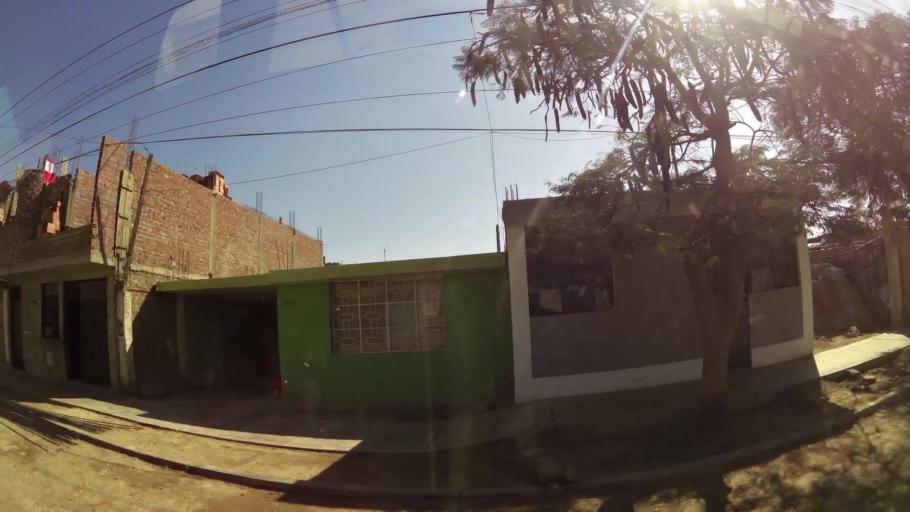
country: PE
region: Ica
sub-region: Provincia de Ica
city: La Tinguina
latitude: -14.0338
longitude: -75.7118
